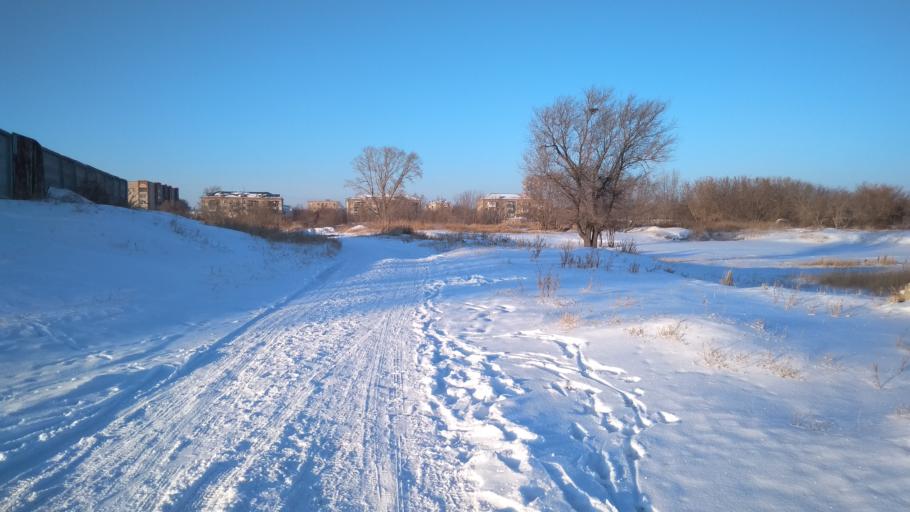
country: RU
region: Chelyabinsk
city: Troitsk
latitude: 54.0816
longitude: 61.5783
